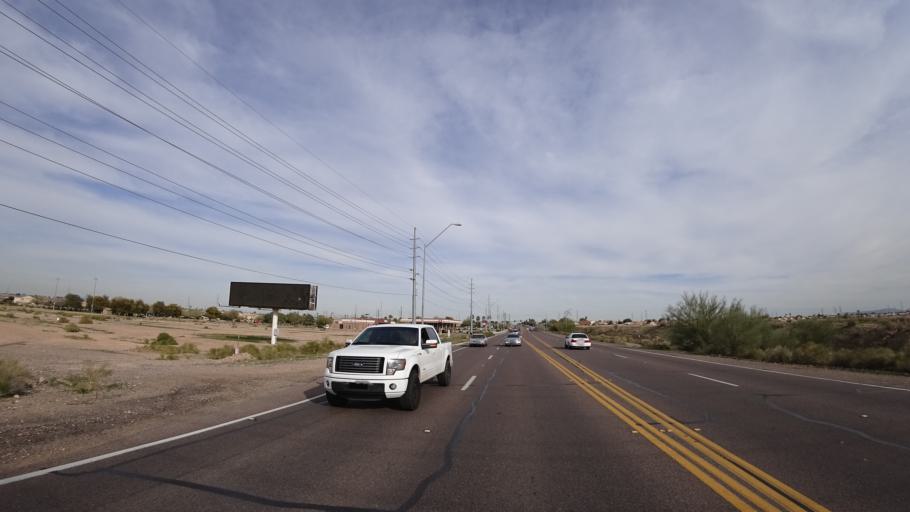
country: US
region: Arizona
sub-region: Maricopa County
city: Youngtown
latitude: 33.5653
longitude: -112.3113
